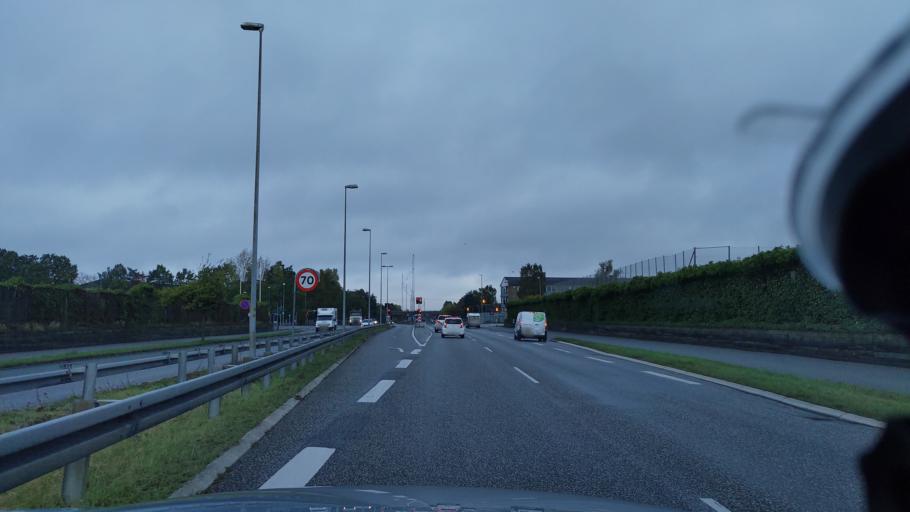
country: DK
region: Capital Region
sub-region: Hvidovre Kommune
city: Hvidovre
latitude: 55.6238
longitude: 12.4738
